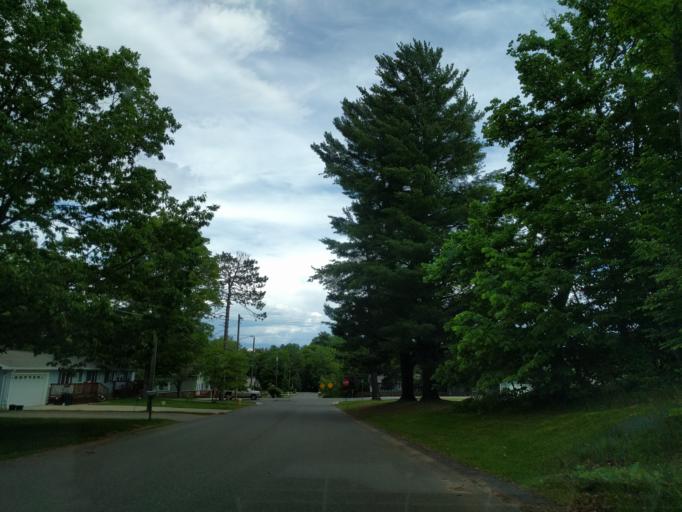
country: US
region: Michigan
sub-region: Marquette County
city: Trowbridge Park
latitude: 46.5542
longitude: -87.4385
